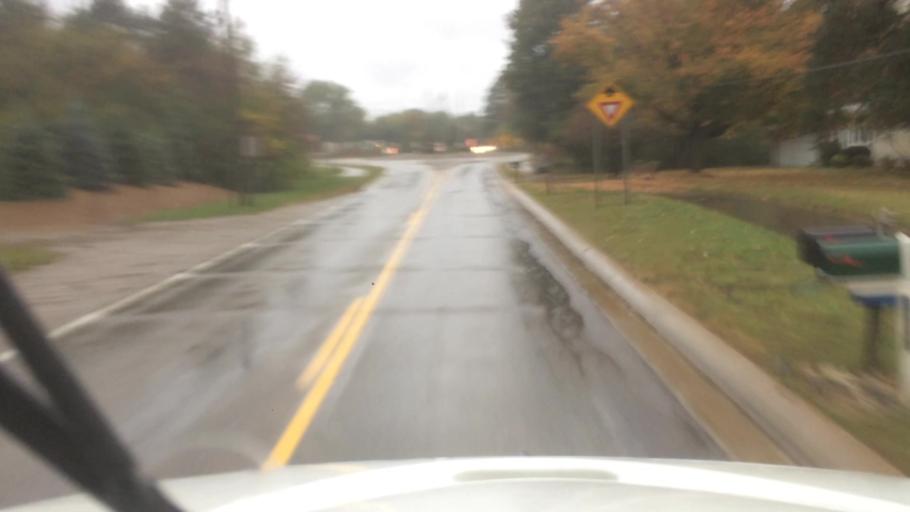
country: US
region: Michigan
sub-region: Oakland County
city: Oxford
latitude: 42.7841
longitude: -83.3180
